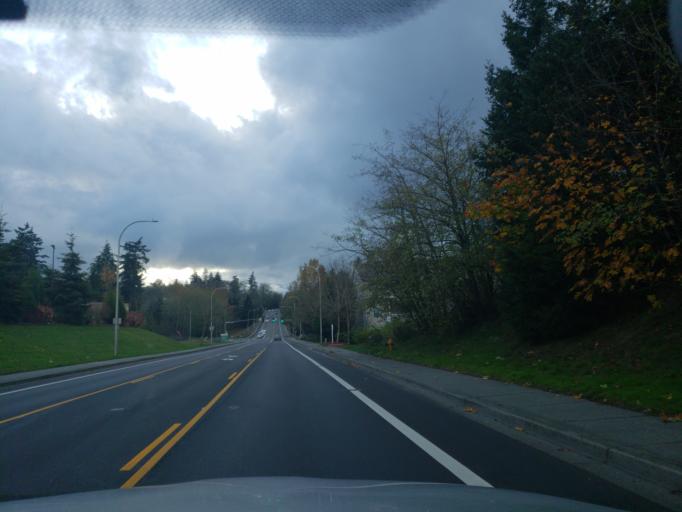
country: US
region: Washington
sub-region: Snohomish County
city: Mukilteo
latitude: 47.9434
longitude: -122.2539
